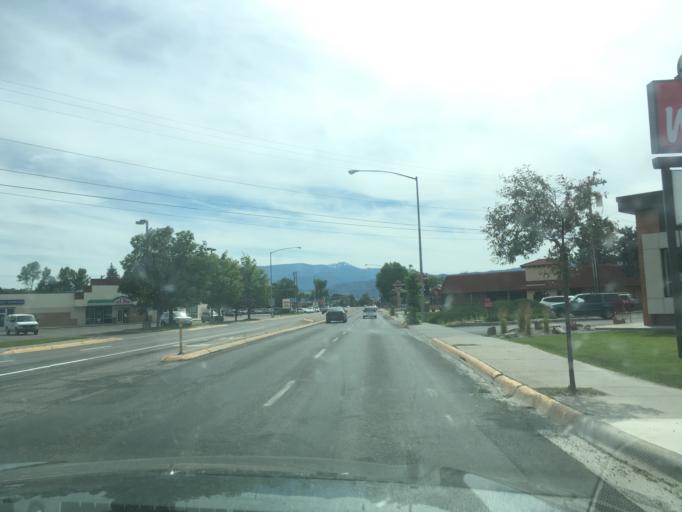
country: US
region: Montana
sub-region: Missoula County
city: Orchard Homes
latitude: 46.8433
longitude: -114.0261
